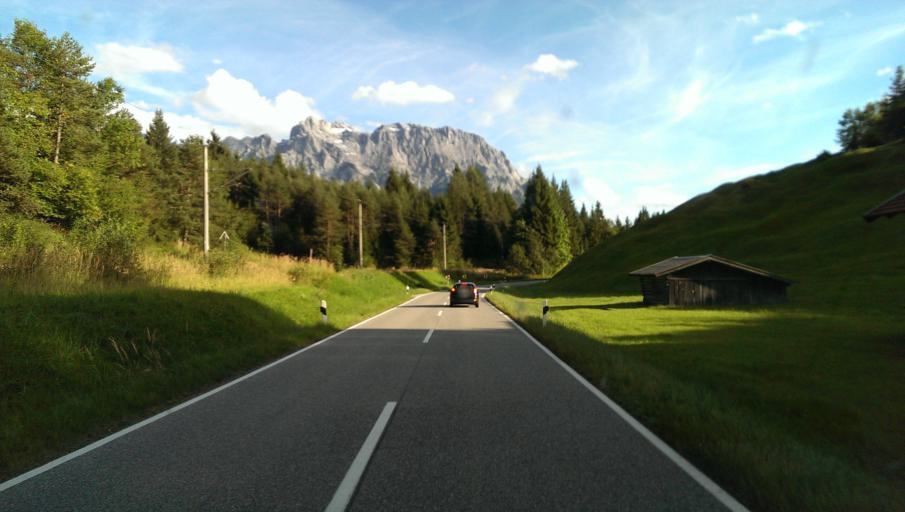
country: DE
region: Bavaria
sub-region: Upper Bavaria
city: Mittenwald
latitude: 47.4719
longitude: 11.2569
